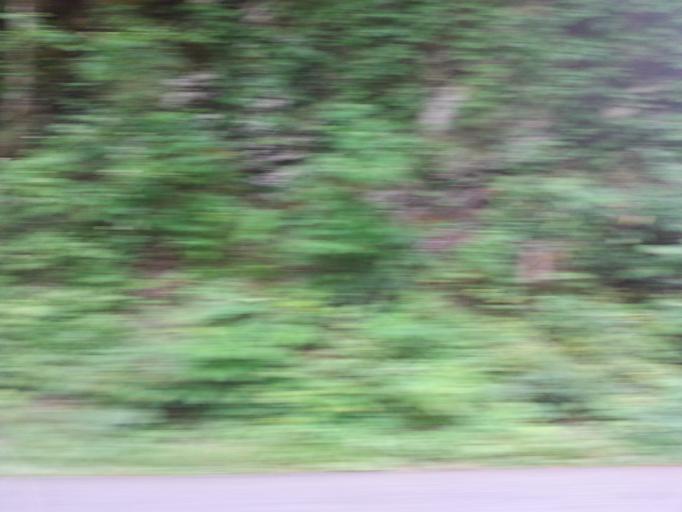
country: US
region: Tennessee
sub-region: Sevier County
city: Pigeon Forge
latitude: 35.6621
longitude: -83.7051
